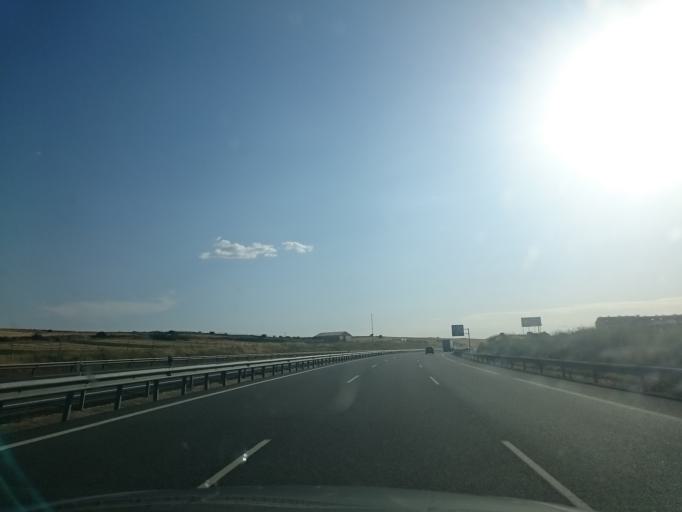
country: ES
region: Castille and Leon
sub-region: Provincia de Burgos
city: Cardenadijo
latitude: 42.3258
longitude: -3.6602
